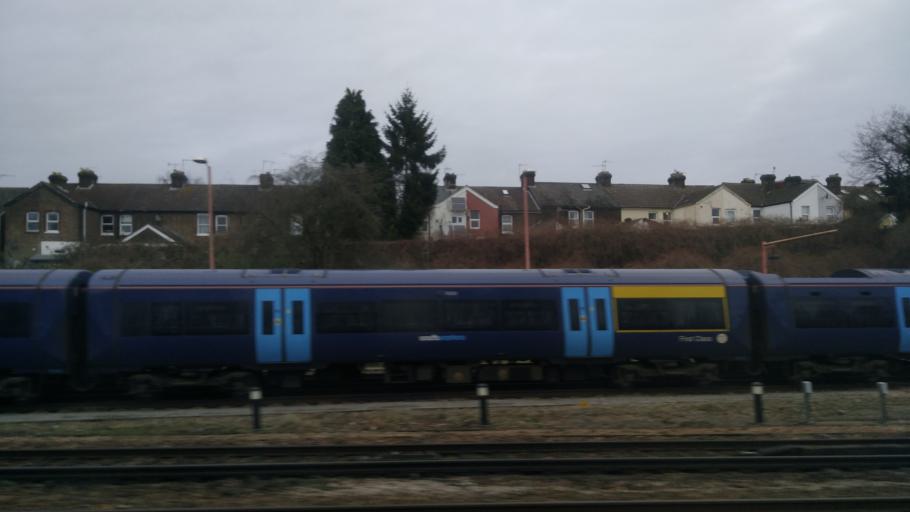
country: GB
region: England
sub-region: Kent
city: Tonbridge
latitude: 51.1928
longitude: 0.2627
